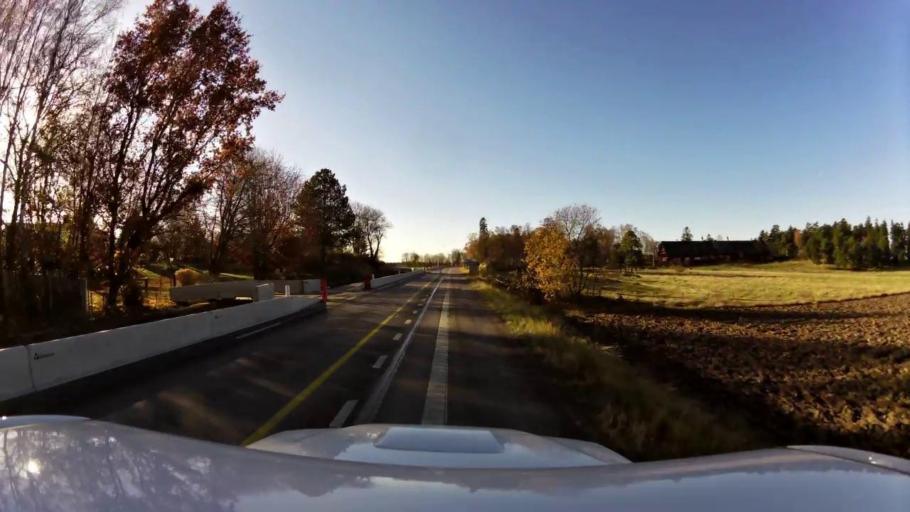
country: SE
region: OEstergoetland
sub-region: Linkopings Kommun
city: Linghem
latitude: 58.4321
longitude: 15.7279
